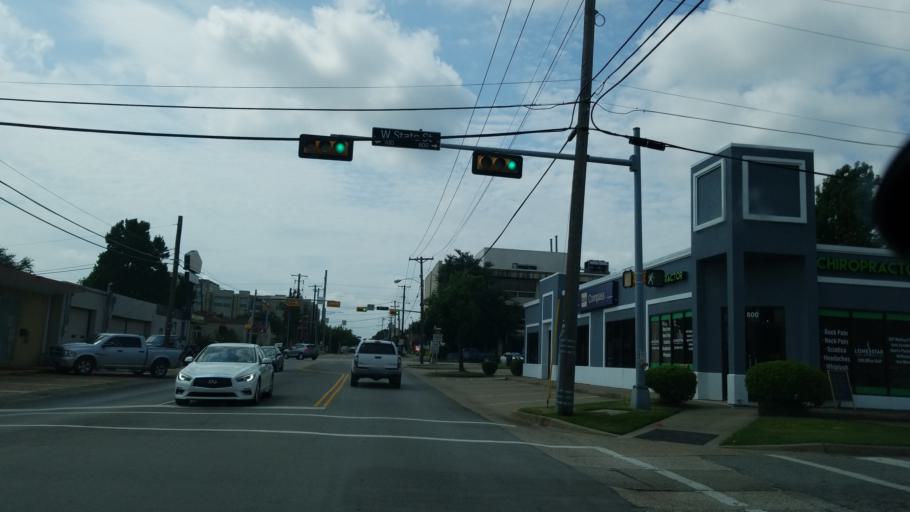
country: US
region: Texas
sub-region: Dallas County
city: Garland
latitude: 32.9135
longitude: -96.6402
